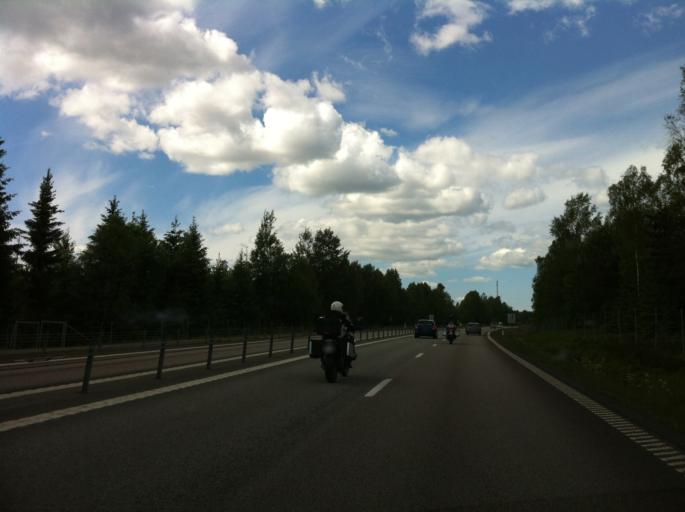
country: SE
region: Vaestra Goetaland
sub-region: Amals Kommun
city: Amal
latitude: 59.0981
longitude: 12.7714
